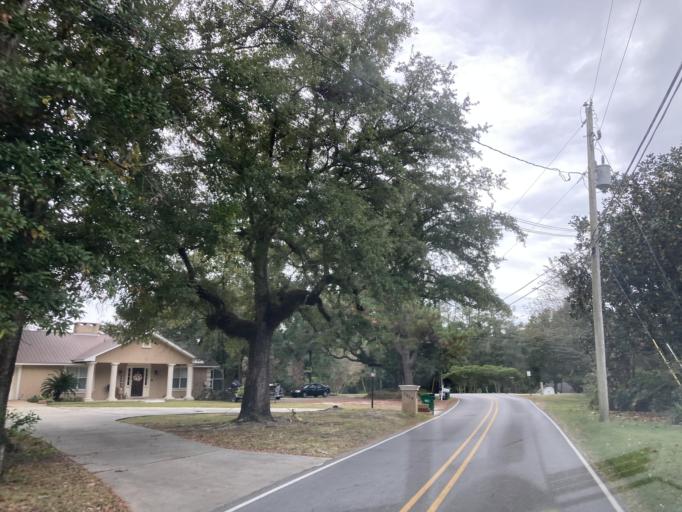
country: US
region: Mississippi
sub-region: Jackson County
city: Gulf Hills
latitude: 30.4281
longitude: -88.8347
